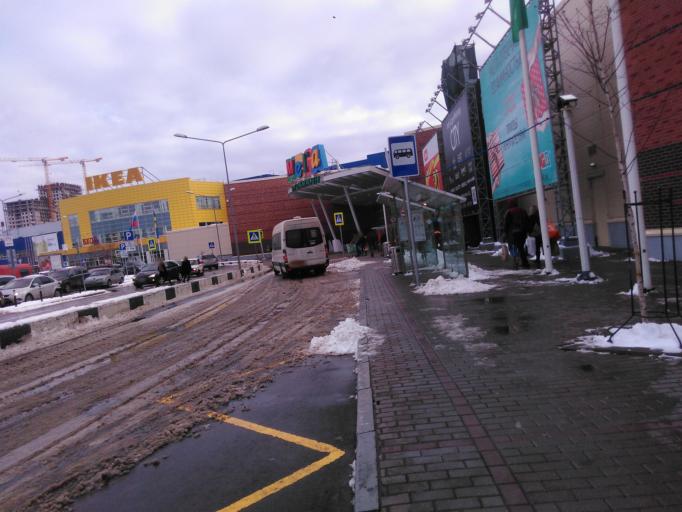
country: RU
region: Moscow
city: Khimki
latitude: 55.9112
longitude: 37.3980
